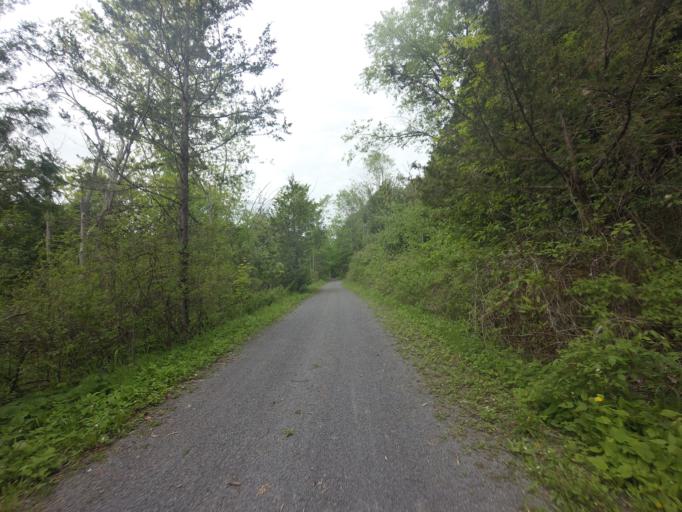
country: CA
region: Ontario
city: Kingston
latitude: 44.3801
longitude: -76.6390
